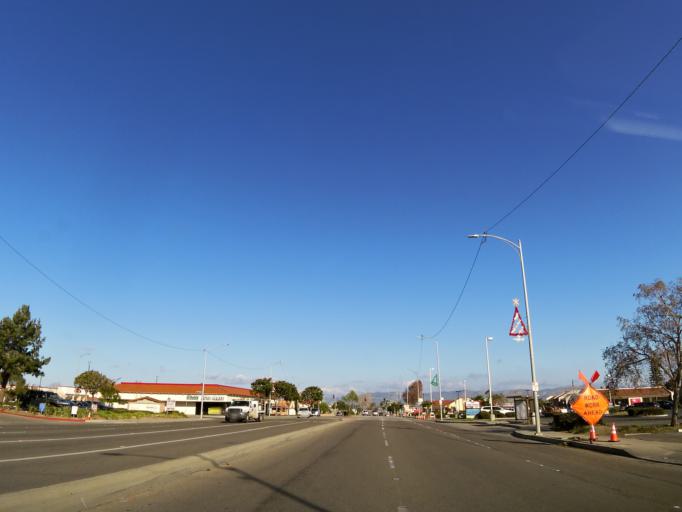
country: US
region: California
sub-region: Santa Barbara County
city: Santa Maria
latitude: 34.9212
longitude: -120.4360
